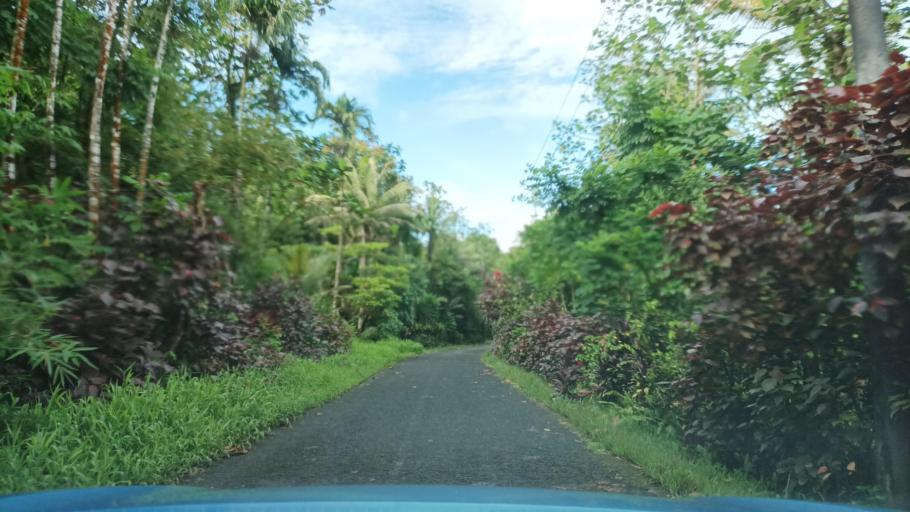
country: FM
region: Pohnpei
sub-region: Sokehs Municipality
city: Palikir - National Government Center
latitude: 6.9148
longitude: 158.1418
